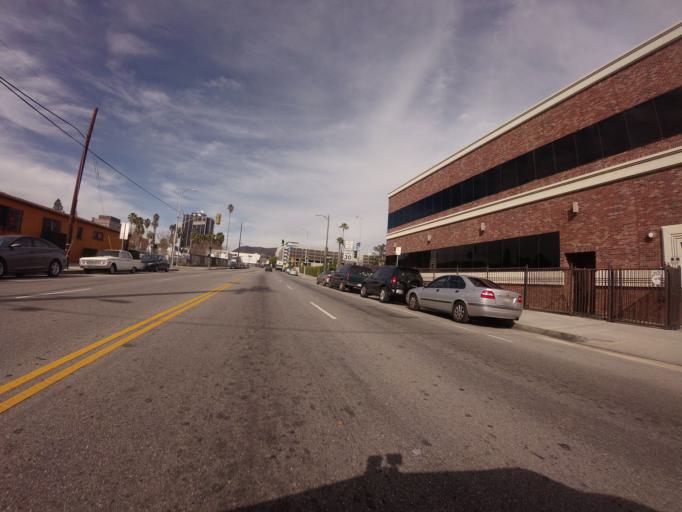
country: US
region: California
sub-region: Los Angeles County
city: Hollywood
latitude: 34.0940
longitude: -118.3288
